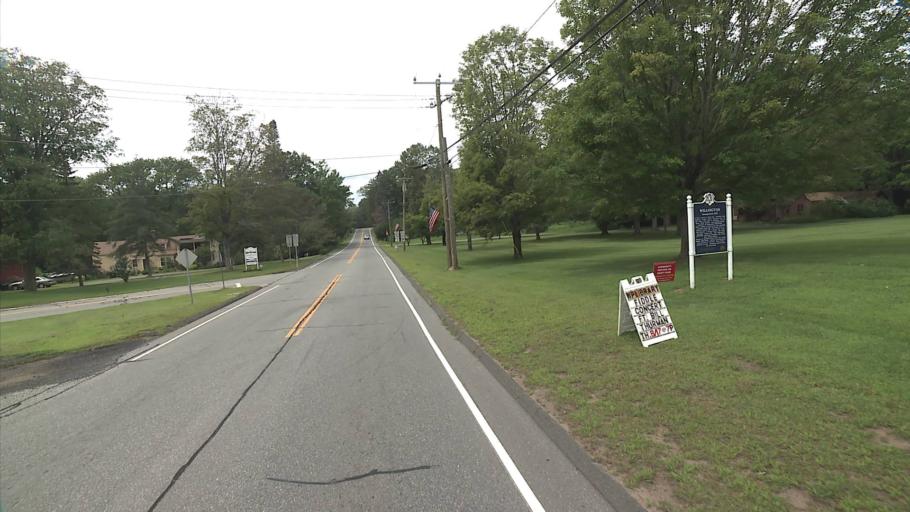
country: US
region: Connecticut
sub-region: Tolland County
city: Storrs
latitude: 41.8755
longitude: -72.2642
